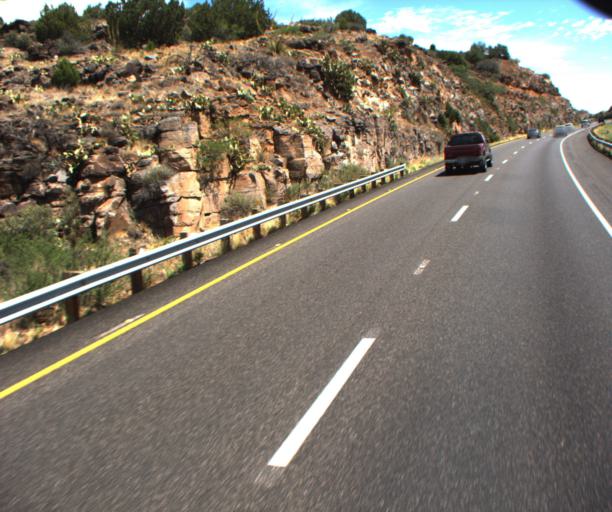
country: US
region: Arizona
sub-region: Yavapai County
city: Big Park
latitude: 34.7157
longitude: -111.7250
